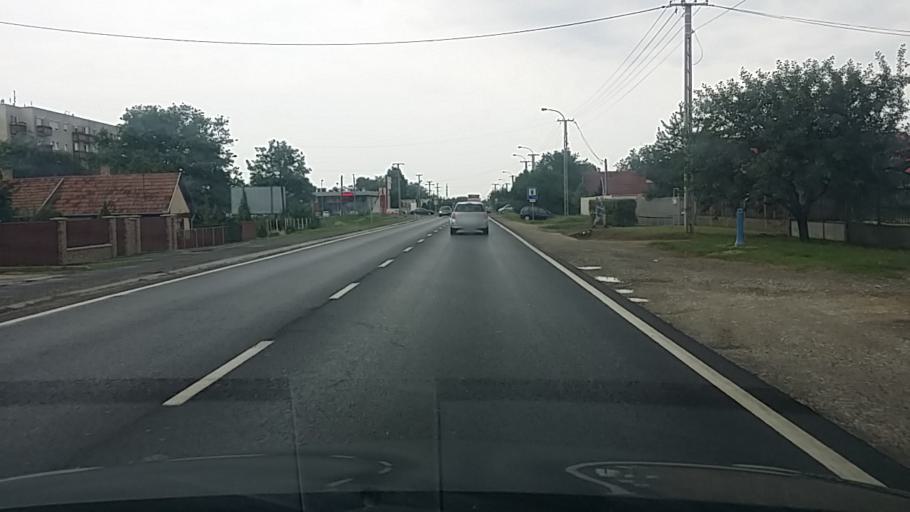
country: HU
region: Szabolcs-Szatmar-Bereg
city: Ujfeherto
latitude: 47.8142
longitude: 21.7015
